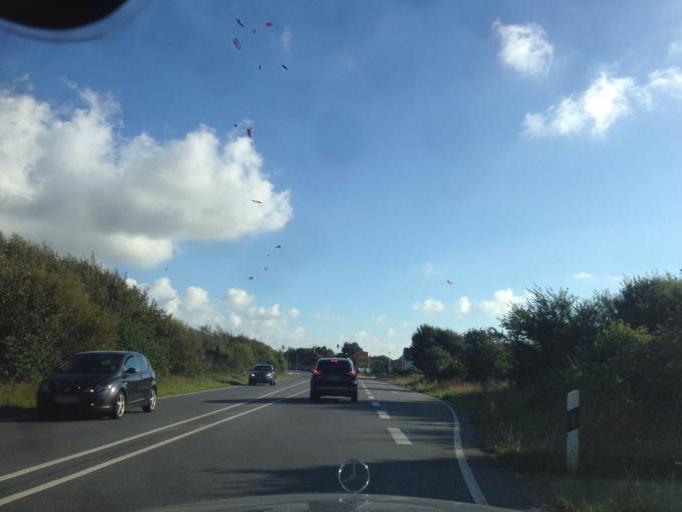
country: DE
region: Schleswig-Holstein
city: Westerland
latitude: 54.9184
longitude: 8.3229
